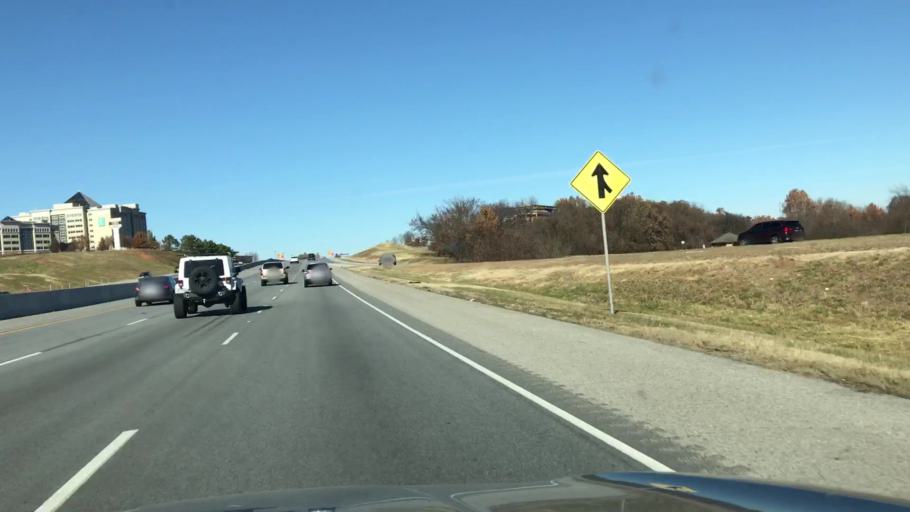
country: US
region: Arkansas
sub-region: Benton County
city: Cave Springs
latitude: 36.3025
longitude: -94.1815
